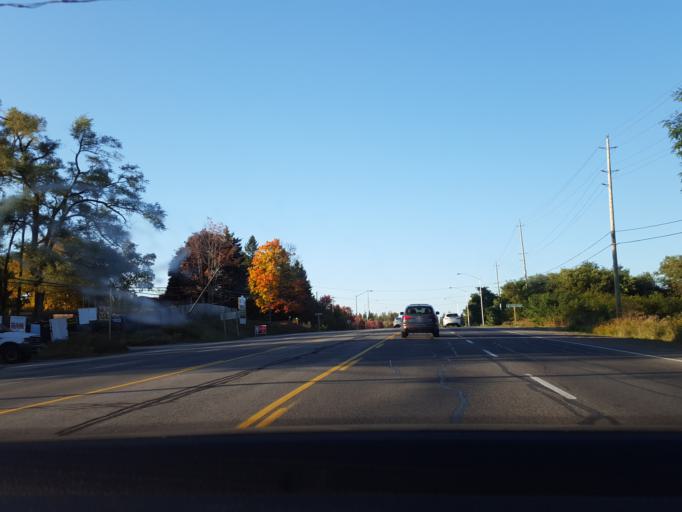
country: CA
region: Ontario
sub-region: York
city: Richmond Hill
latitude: 43.9575
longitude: -79.4576
